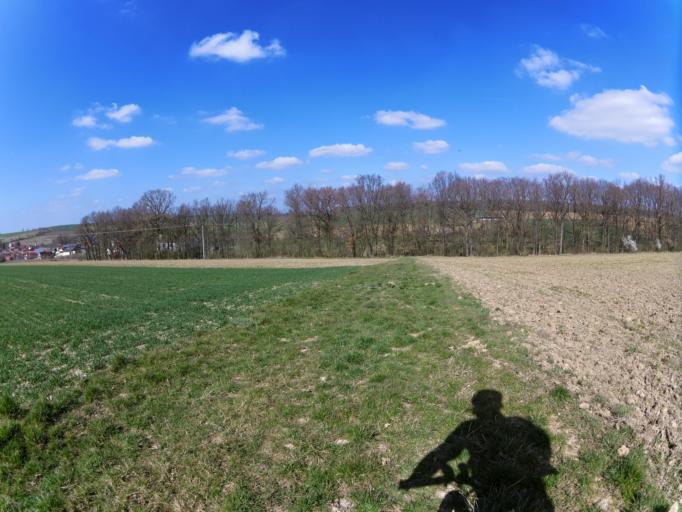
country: DE
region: Bavaria
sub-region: Regierungsbezirk Unterfranken
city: Prosselsheim
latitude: 49.8402
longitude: 10.1532
